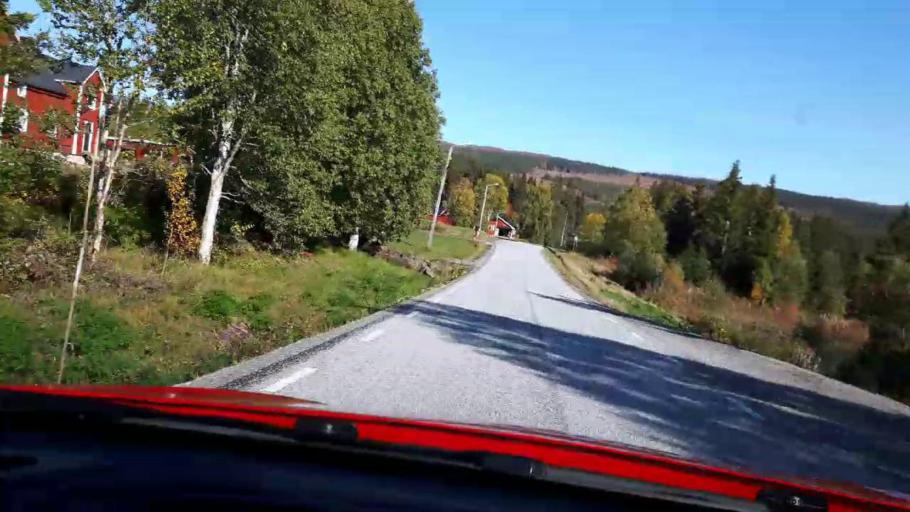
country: NO
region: Nord-Trondelag
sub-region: Royrvik
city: Royrvik
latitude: 64.7310
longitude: 14.0013
